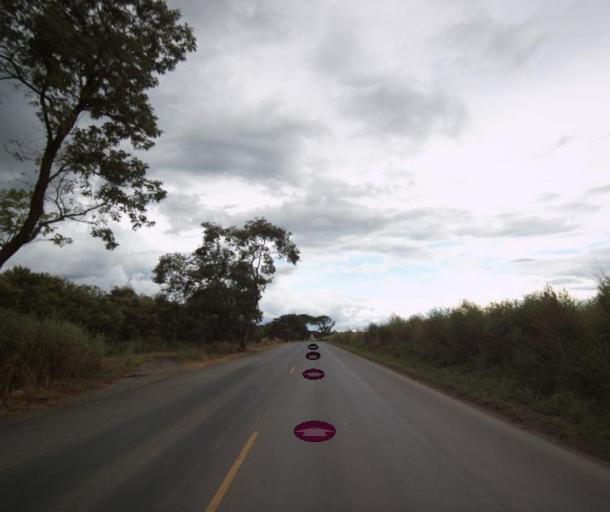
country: BR
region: Goias
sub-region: Itapaci
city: Itapaci
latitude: -14.9797
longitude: -49.3968
